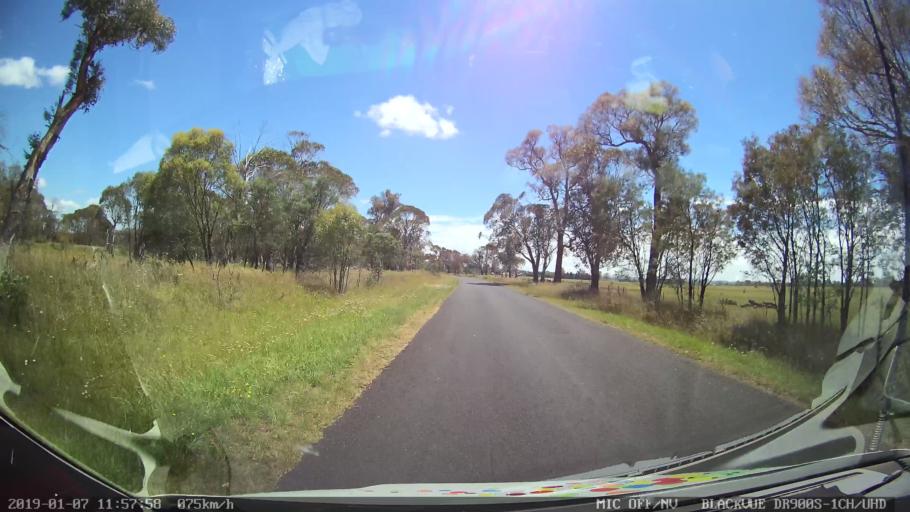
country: AU
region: New South Wales
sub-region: Guyra
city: Guyra
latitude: -30.2585
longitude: 151.6668
